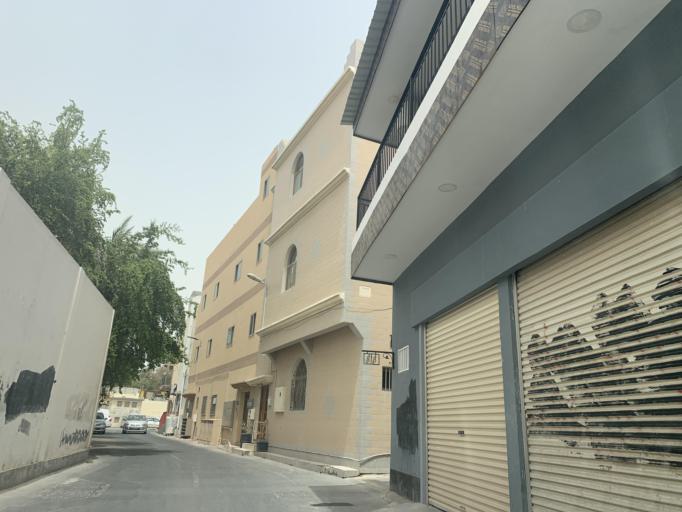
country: BH
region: Manama
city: Jidd Hafs
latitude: 26.2305
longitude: 50.5271
